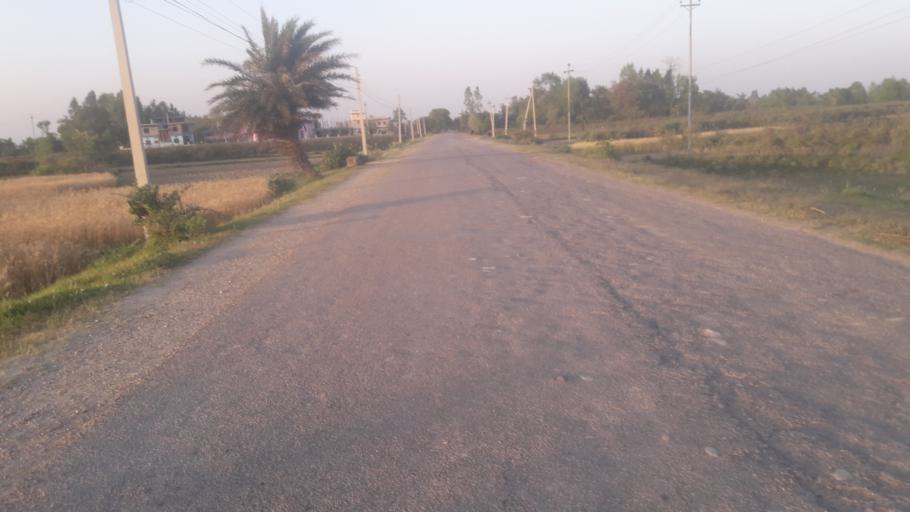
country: NP
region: Eastern Region
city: Siraha
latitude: 26.6323
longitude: 86.1971
